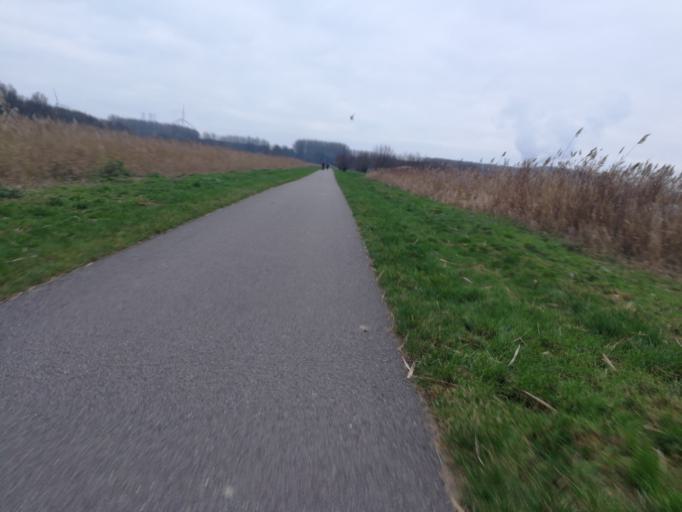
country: NL
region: South Holland
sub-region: Gemeente Vlaardingen
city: Vlaardingen
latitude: 51.9153
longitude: 4.3019
